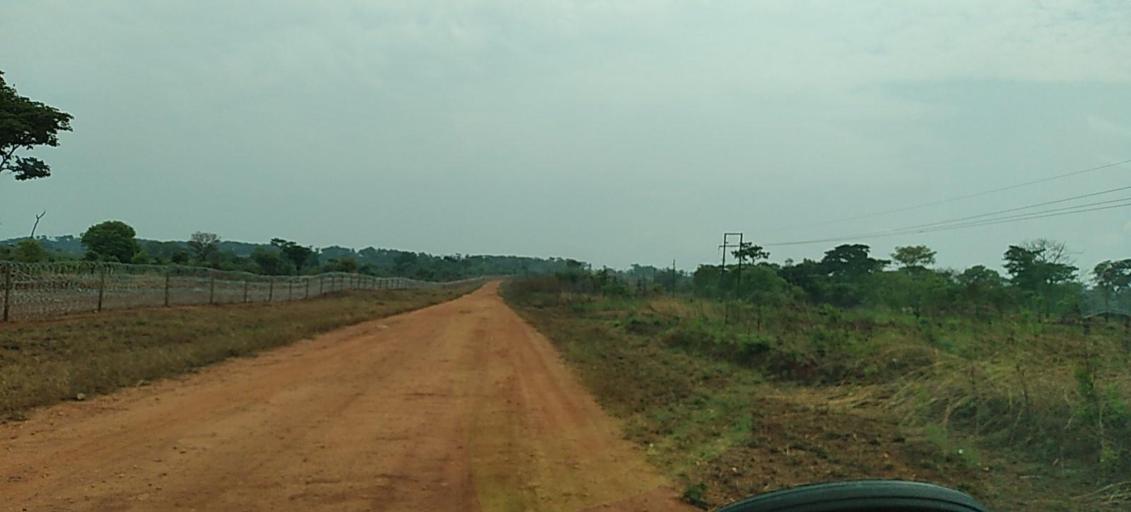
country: ZM
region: North-Western
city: Kansanshi
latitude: -12.1068
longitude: 26.4906
